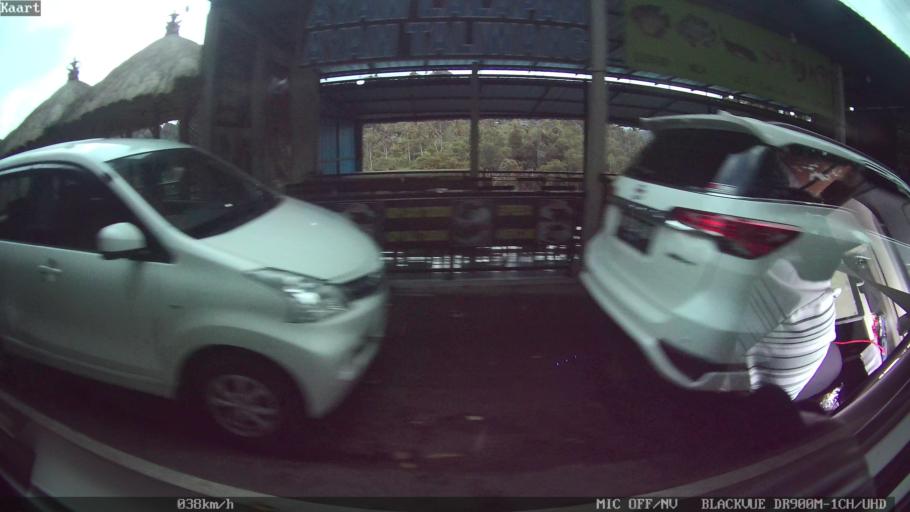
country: ID
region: Bali
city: Petang
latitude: -8.3706
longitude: 115.2243
